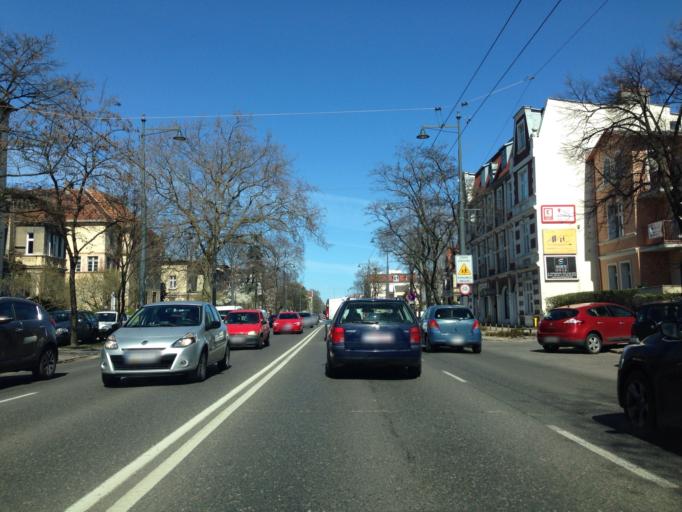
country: PL
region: Pomeranian Voivodeship
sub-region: Sopot
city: Sopot
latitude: 54.4365
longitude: 18.5611
